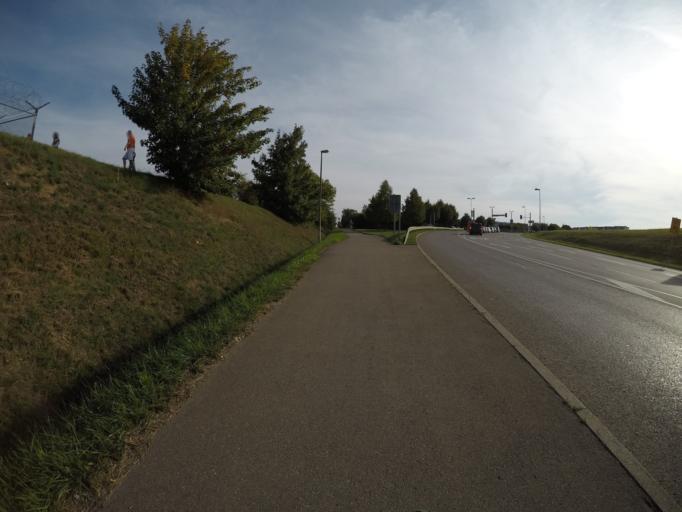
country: DE
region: Baden-Wuerttemberg
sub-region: Regierungsbezirk Stuttgart
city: Filderstadt
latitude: 48.6872
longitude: 9.2184
